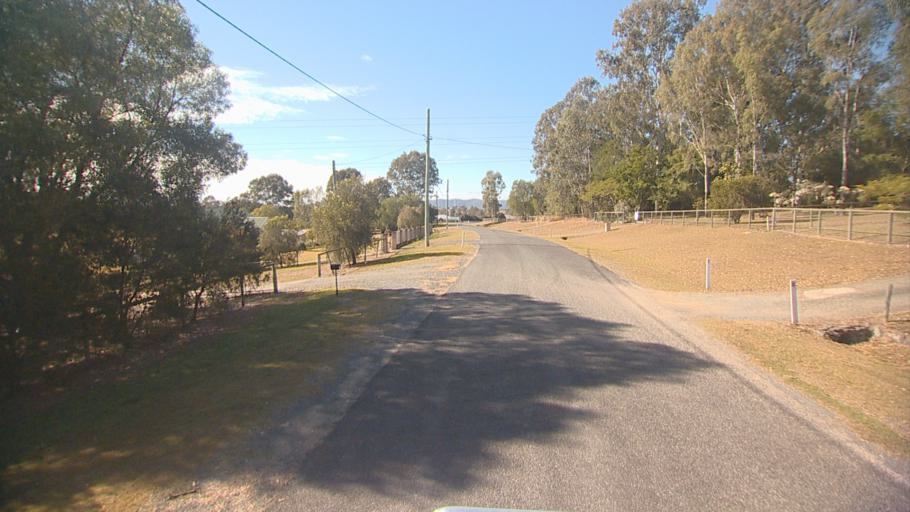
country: AU
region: Queensland
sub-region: Logan
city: Chambers Flat
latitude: -27.7715
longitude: 153.0786
